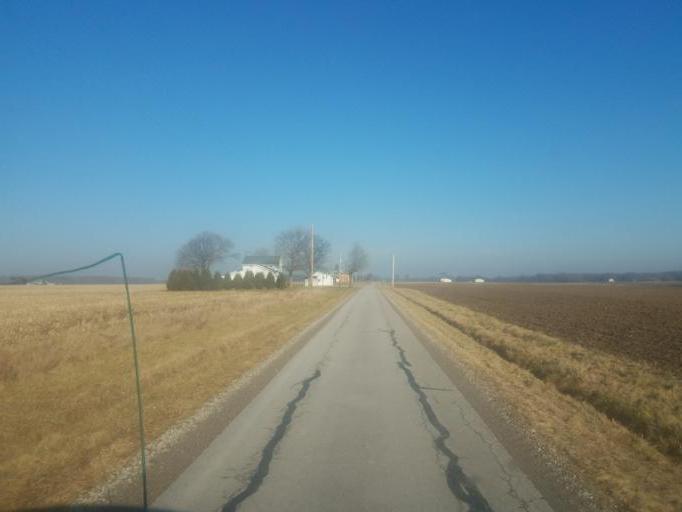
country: US
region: Ohio
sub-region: Huron County
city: Willard
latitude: 41.0279
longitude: -82.9391
